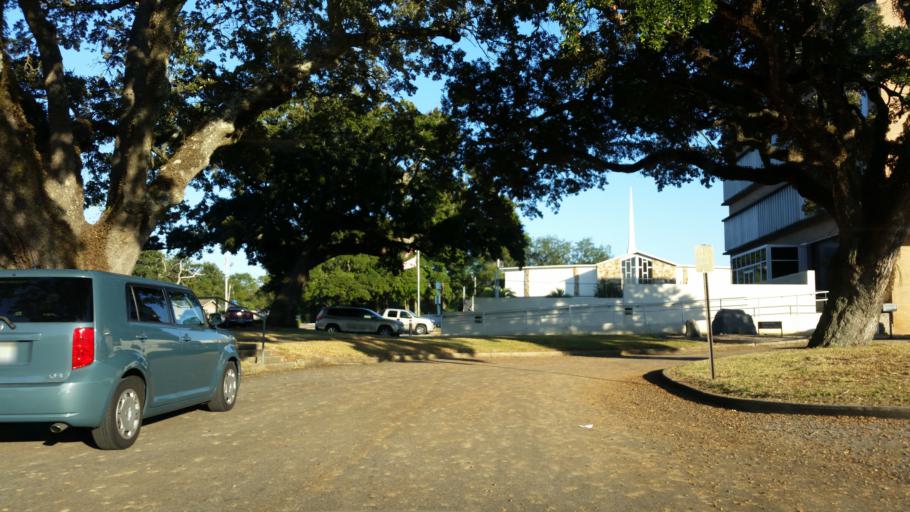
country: US
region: Florida
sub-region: Escambia County
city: Pensacola
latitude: 30.4137
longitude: -87.2425
